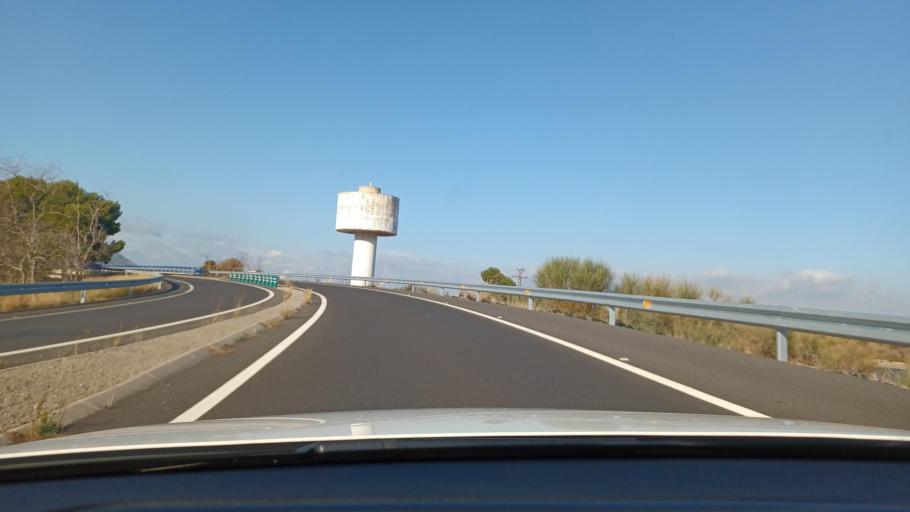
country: ES
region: Valencia
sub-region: Provincia de Castello
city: Moncofar
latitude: 39.8100
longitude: -0.1566
